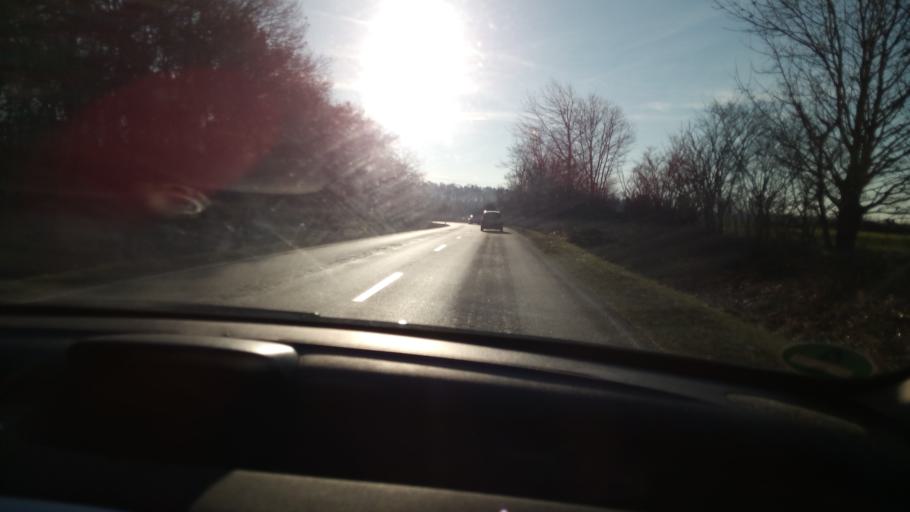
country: DE
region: Schleswig-Holstein
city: Buchhorst
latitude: 53.3962
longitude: 10.5559
